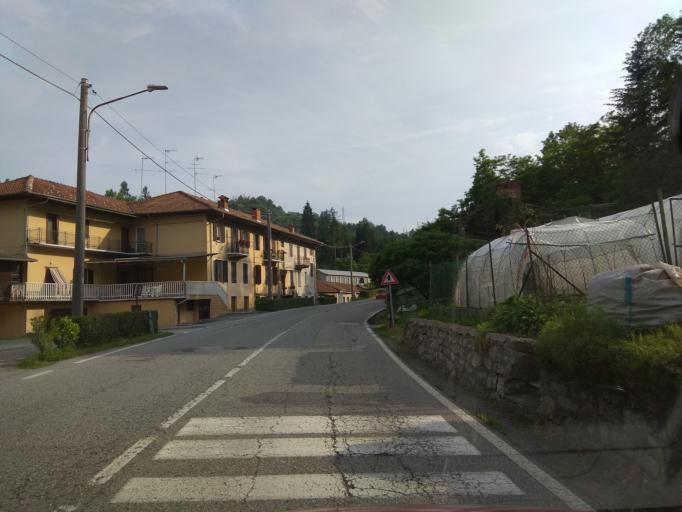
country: IT
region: Piedmont
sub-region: Provincia di Biella
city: Lanvario
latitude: 45.6568
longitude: 8.1976
